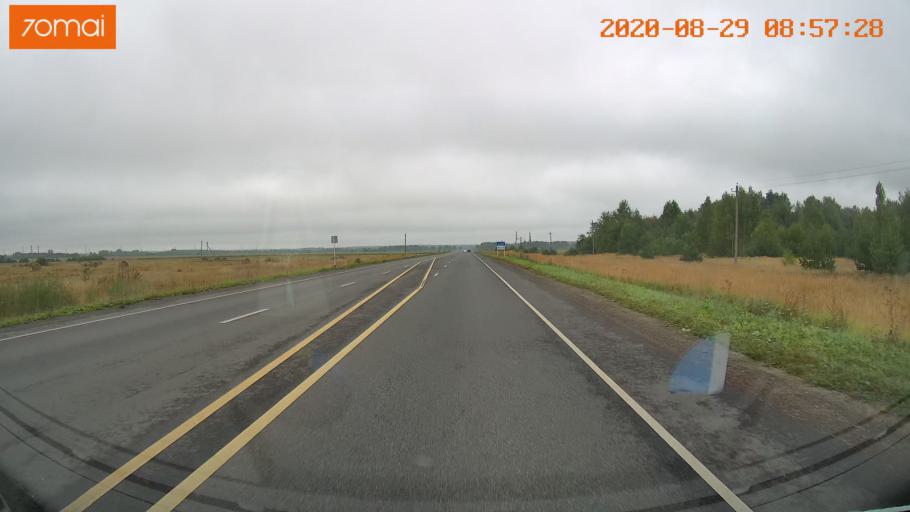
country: RU
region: Ivanovo
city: Staraya Vichuga
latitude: 57.2642
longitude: 41.9045
